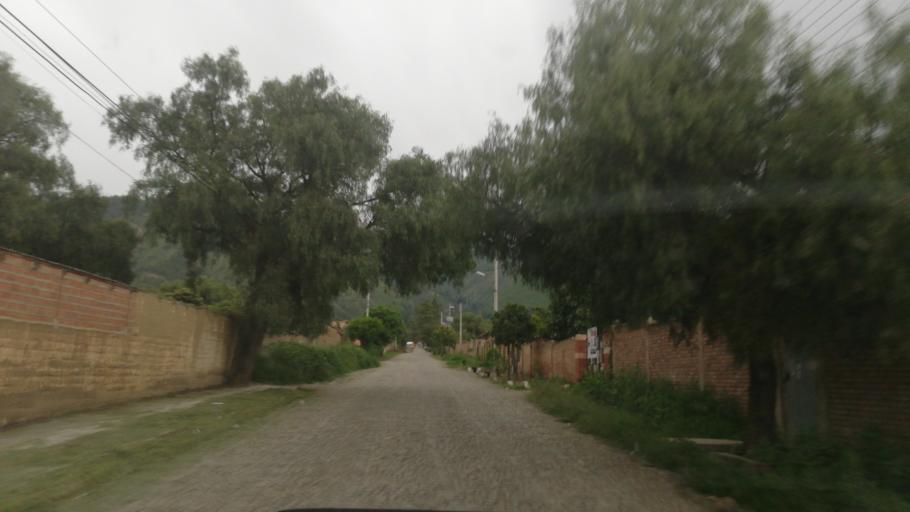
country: BO
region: Cochabamba
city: Cochabamba
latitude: -17.3319
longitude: -66.2159
